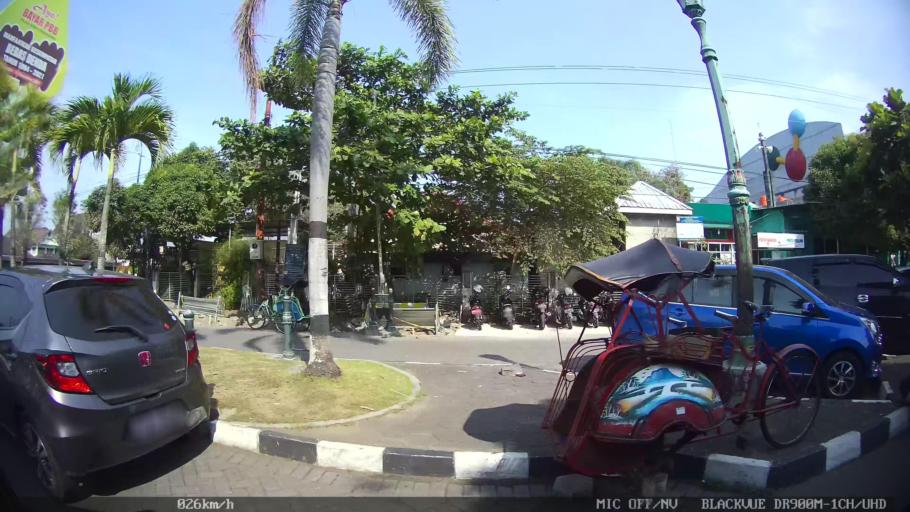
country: ID
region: Daerah Istimewa Yogyakarta
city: Yogyakarta
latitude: -7.8011
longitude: 110.3671
